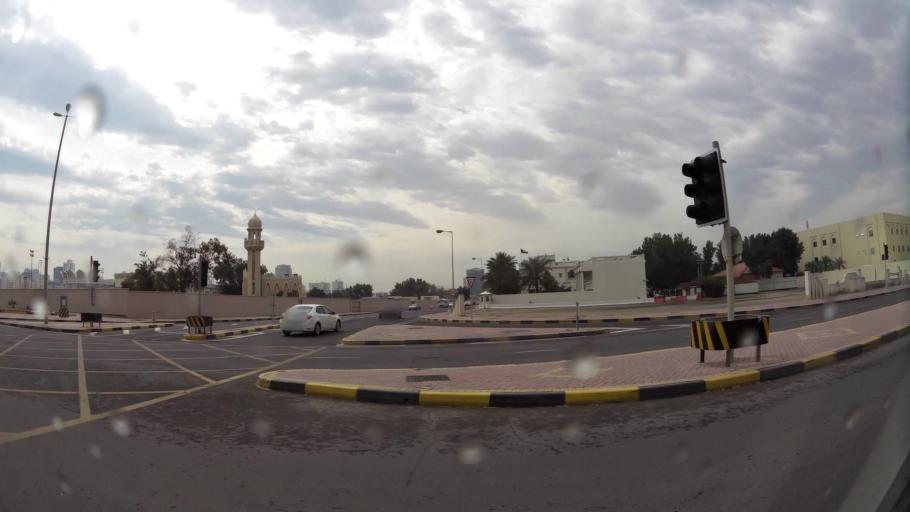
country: BH
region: Manama
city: Manama
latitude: 26.2243
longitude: 50.5950
